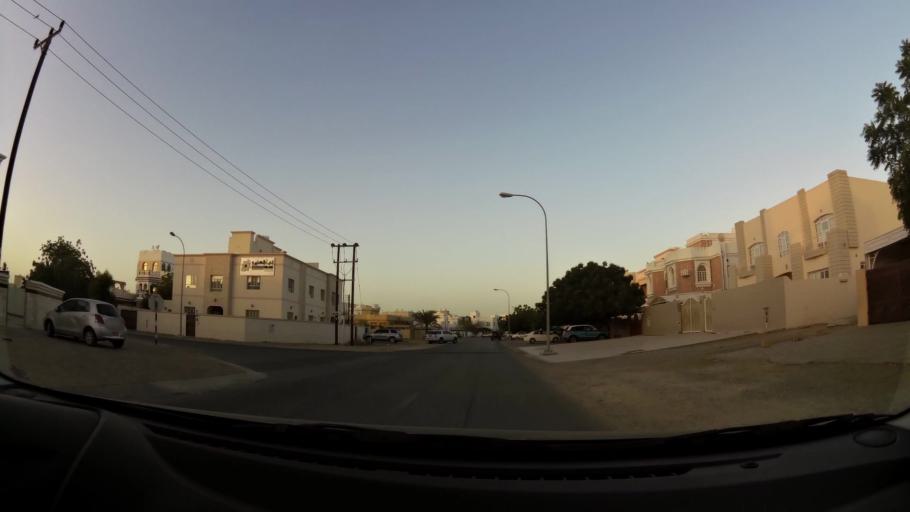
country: OM
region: Muhafazat Masqat
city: As Sib al Jadidah
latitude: 23.5962
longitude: 58.2377
